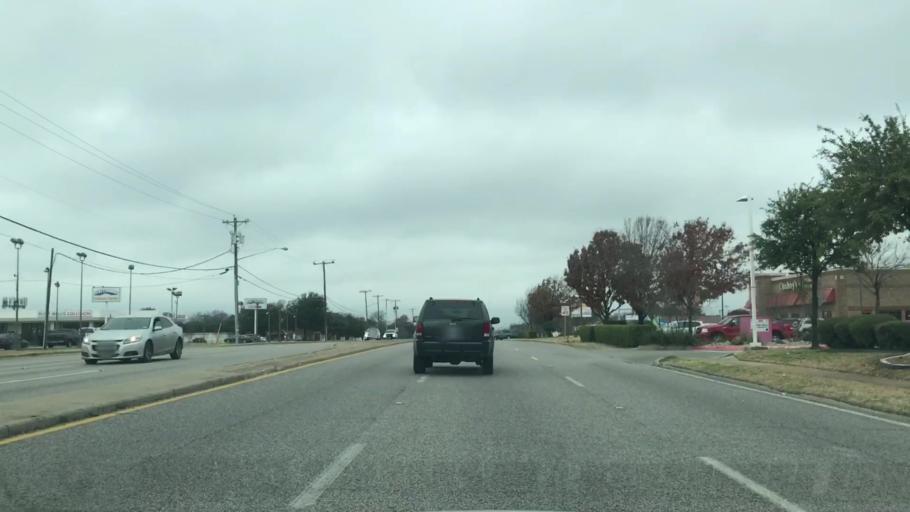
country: US
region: Texas
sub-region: Dallas County
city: Garland
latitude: 32.8642
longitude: -96.6835
